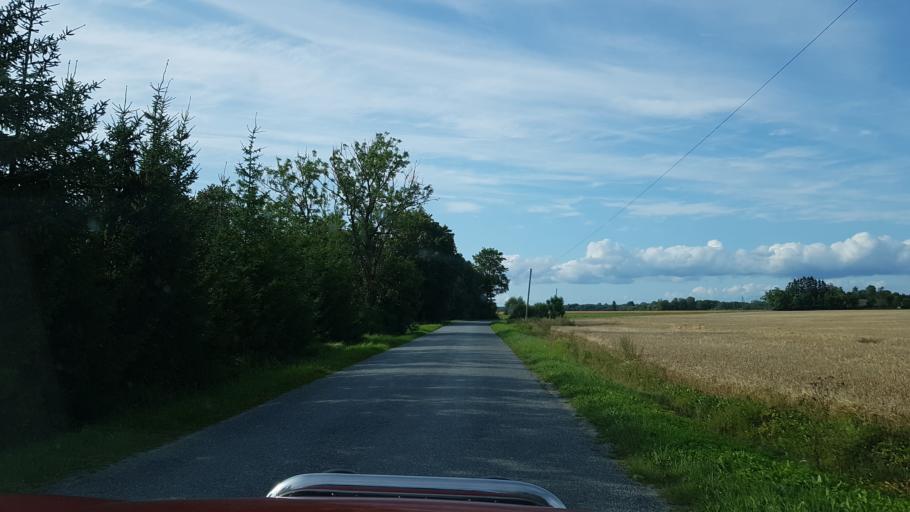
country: EE
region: Laeaene
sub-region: Lihula vald
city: Lihula
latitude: 58.4500
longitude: 23.9972
